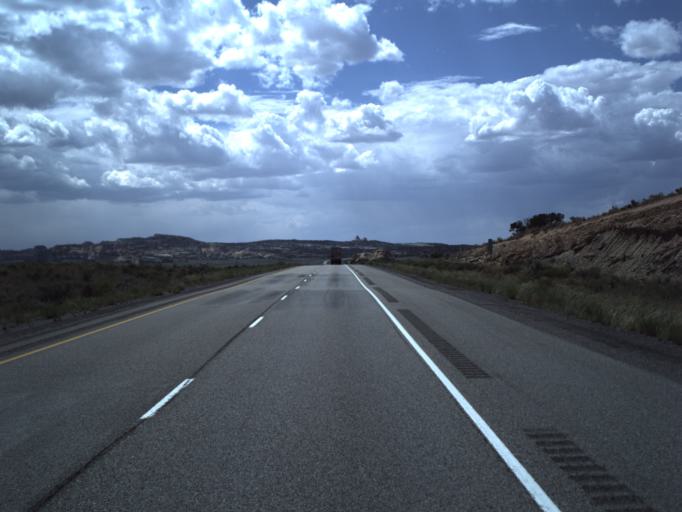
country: US
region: Utah
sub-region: Emery County
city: Castle Dale
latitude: 38.8741
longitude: -110.7549
